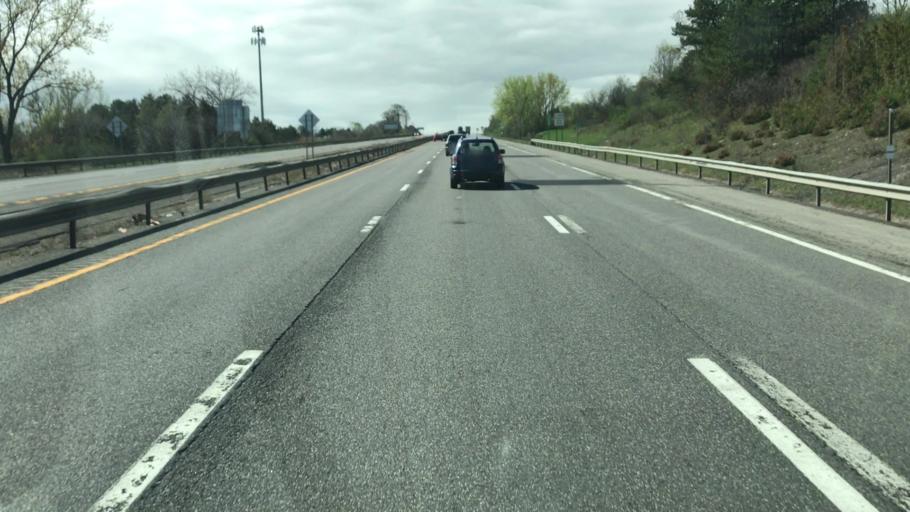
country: US
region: New York
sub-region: Onondaga County
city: Nedrow
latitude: 42.8894
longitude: -76.1096
